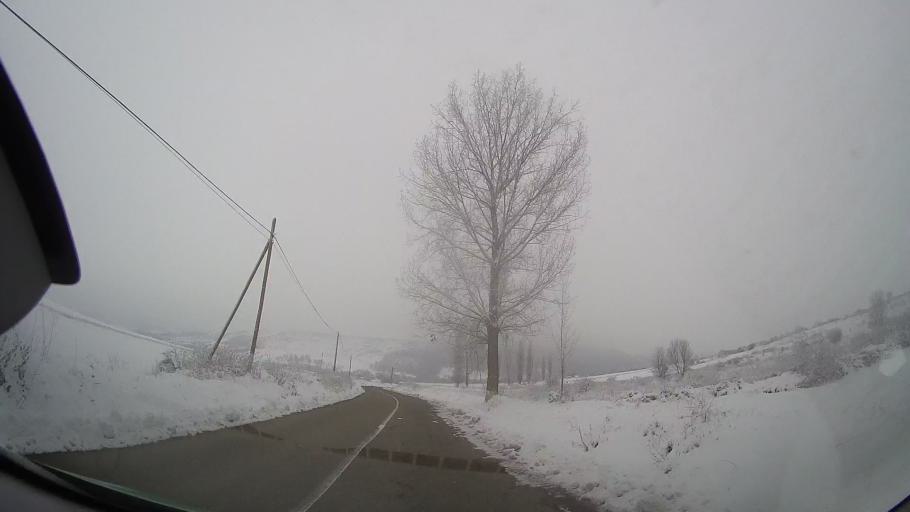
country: RO
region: Neamt
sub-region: Comuna Bozieni
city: Bozieni
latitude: 46.8442
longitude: 27.1687
